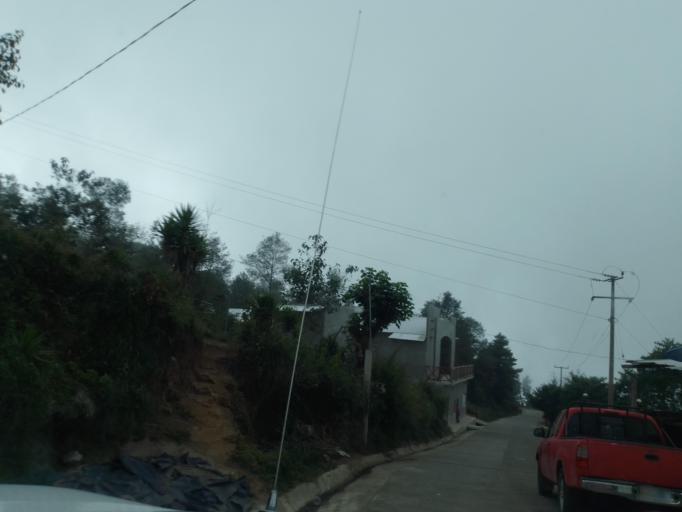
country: MX
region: Chiapas
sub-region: Union Juarez
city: Santo Domingo
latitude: 15.0884
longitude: -92.0915
